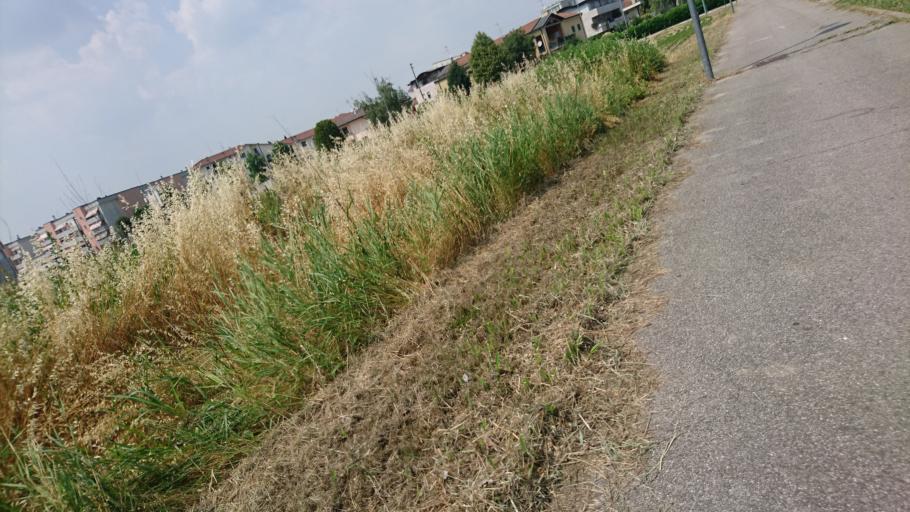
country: IT
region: Veneto
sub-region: Provincia di Padova
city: Masera di Padova
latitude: 45.3150
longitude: 11.8673
